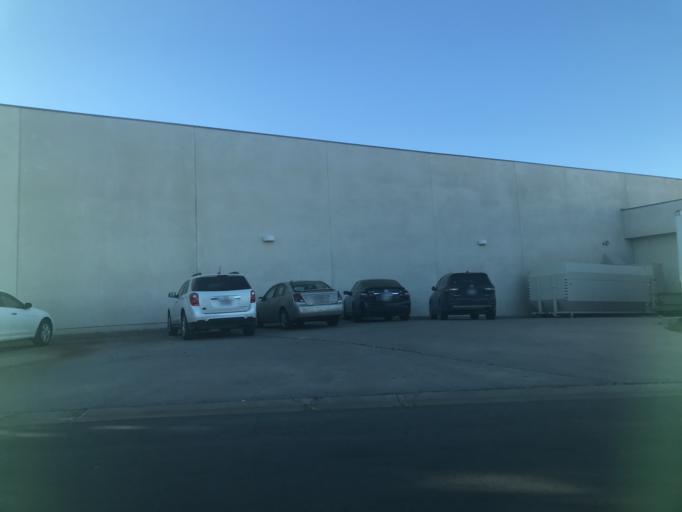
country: US
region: Texas
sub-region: Tom Green County
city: San Angelo
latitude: 31.4265
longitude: -100.4983
